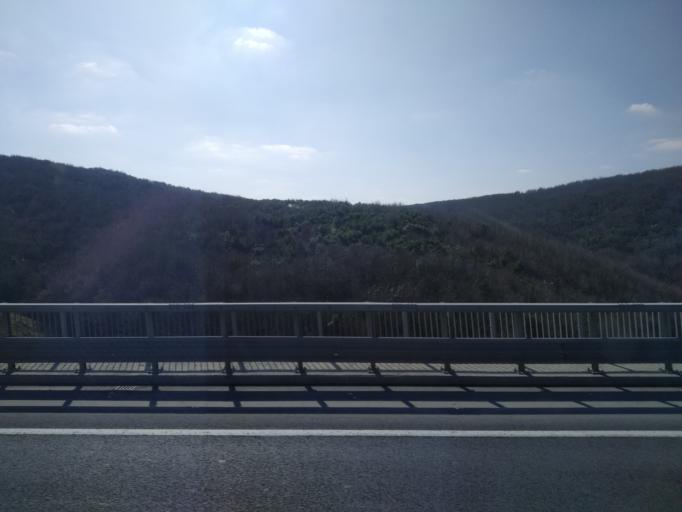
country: TR
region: Istanbul
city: Arikoey
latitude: 41.2302
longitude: 28.9714
